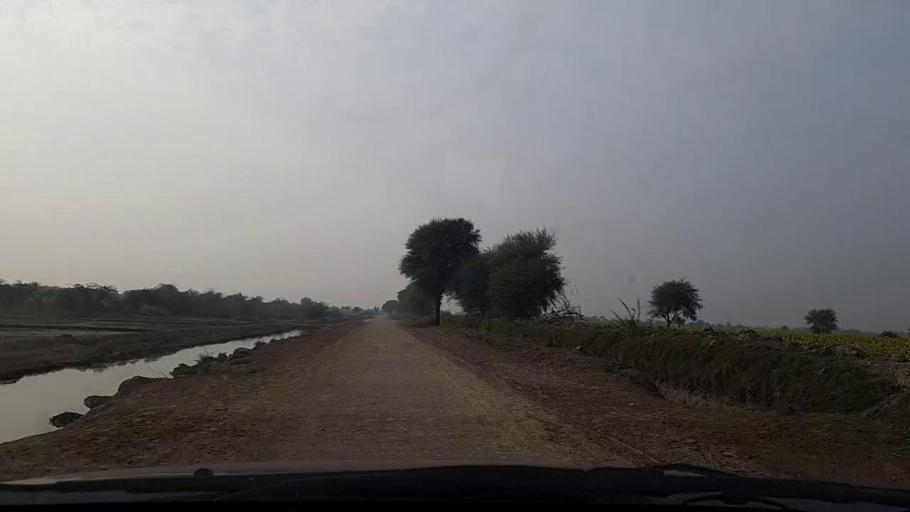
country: PK
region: Sindh
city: Pithoro
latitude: 25.7216
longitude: 69.3932
